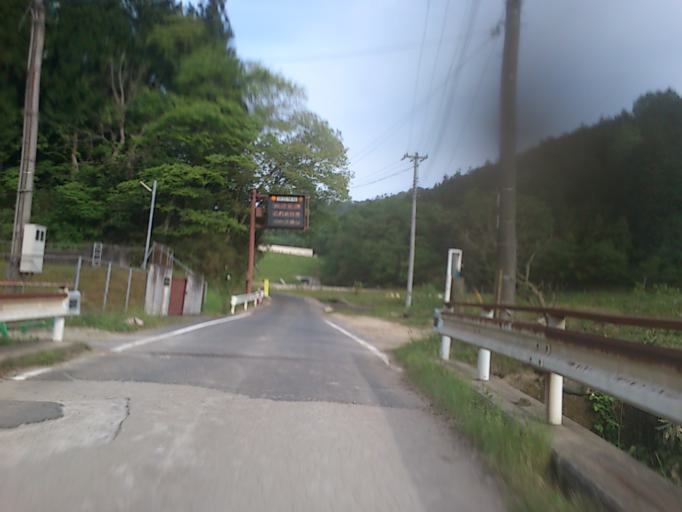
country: JP
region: Kyoto
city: Miyazu
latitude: 35.5680
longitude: 135.1180
